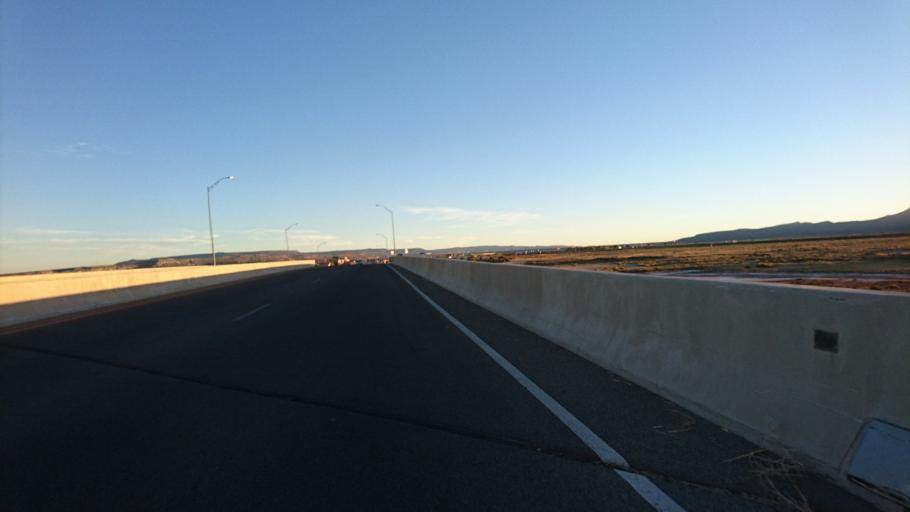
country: US
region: New Mexico
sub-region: Cibola County
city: Grants
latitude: 35.1377
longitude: -107.8282
